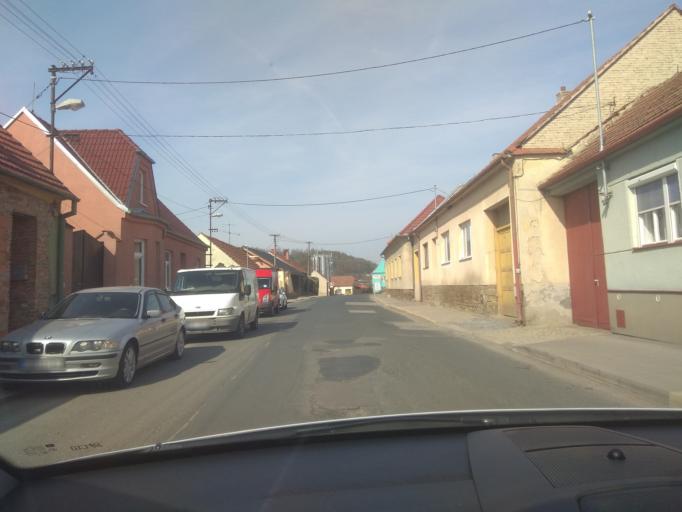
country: CZ
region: South Moravian
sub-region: Okres Brno-Venkov
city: Rosice
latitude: 49.1796
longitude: 16.3895
